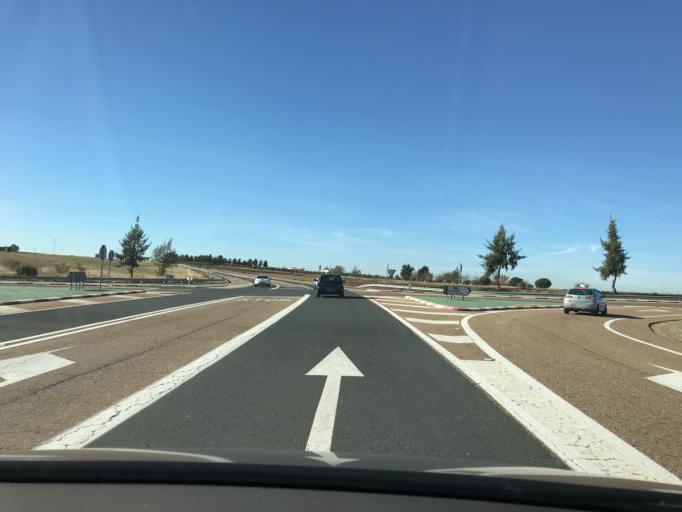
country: ES
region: Extremadura
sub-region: Provincia de Badajoz
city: Azuaga
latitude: 38.2764
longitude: -5.6768
